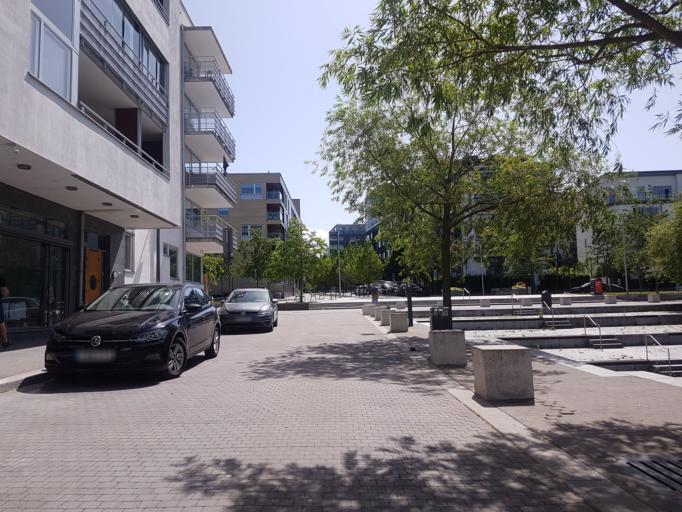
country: SE
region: Stockholm
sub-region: Stockholms Kommun
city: OEstermalm
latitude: 59.3049
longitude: 18.0906
